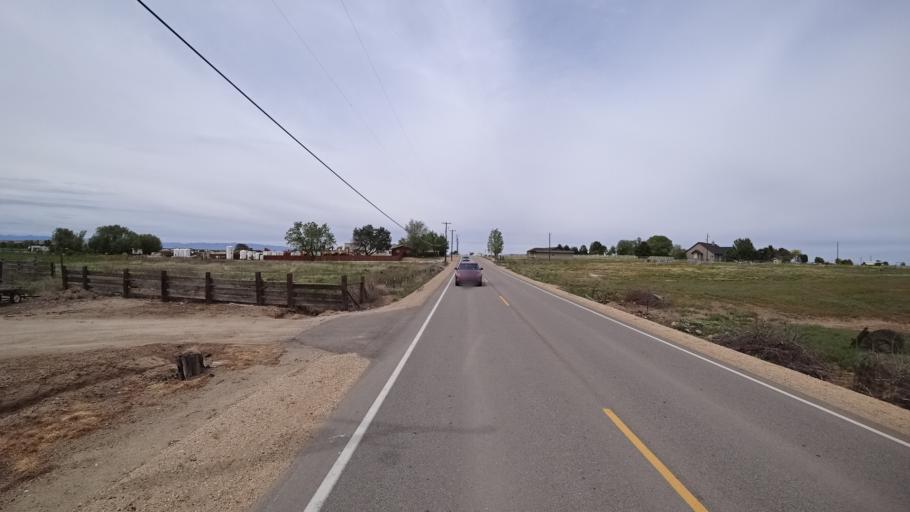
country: US
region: Idaho
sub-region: Ada County
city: Kuna
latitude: 43.5319
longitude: -116.3632
